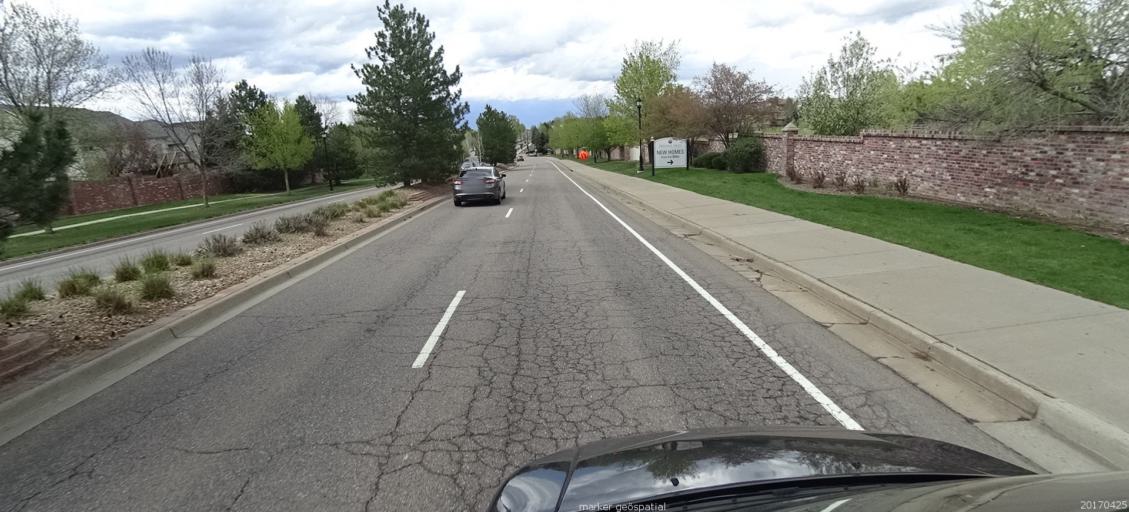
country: US
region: Colorado
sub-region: Adams County
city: Lone Tree
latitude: 39.5444
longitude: -104.8855
